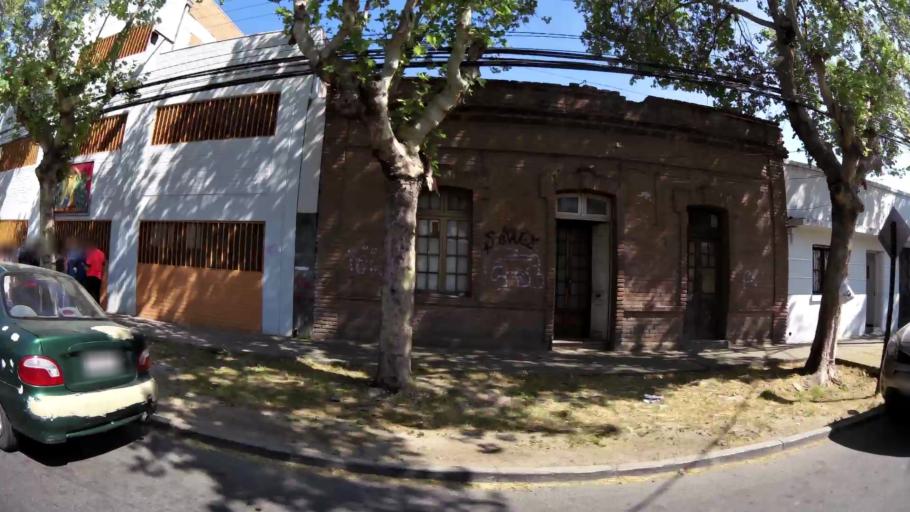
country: CL
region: Santiago Metropolitan
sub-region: Provincia de Maipo
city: San Bernardo
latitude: -33.5879
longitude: -70.7037
